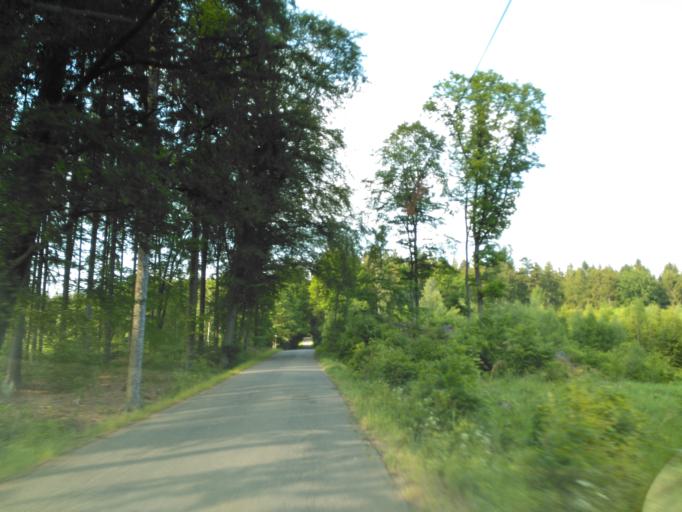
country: CZ
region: Plzensky
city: Zbiroh
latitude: 49.9042
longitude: 13.8149
